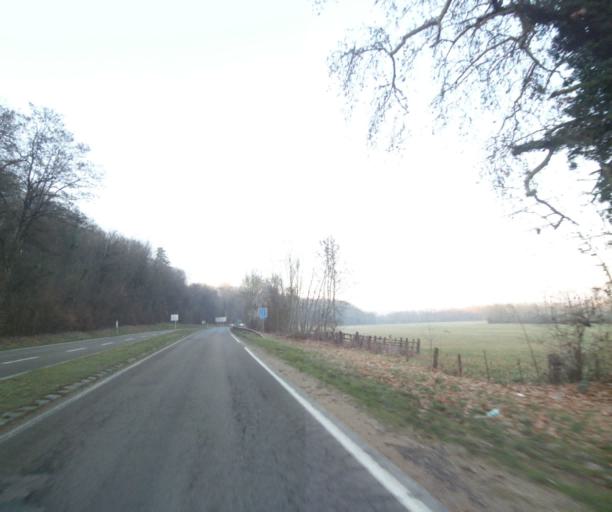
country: FR
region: Champagne-Ardenne
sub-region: Departement de la Haute-Marne
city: Bienville
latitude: 48.5930
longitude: 5.0312
